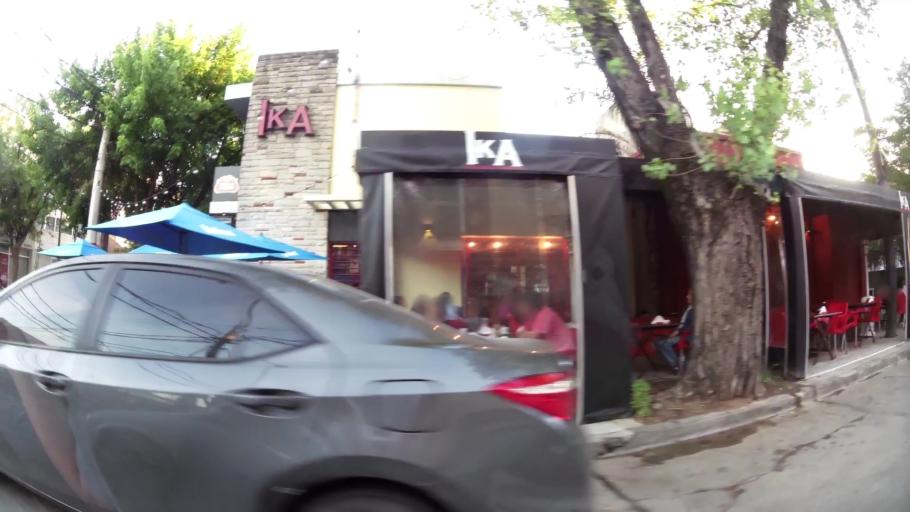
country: AR
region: Buenos Aires
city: Ituzaingo
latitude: -34.6486
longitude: -58.6422
